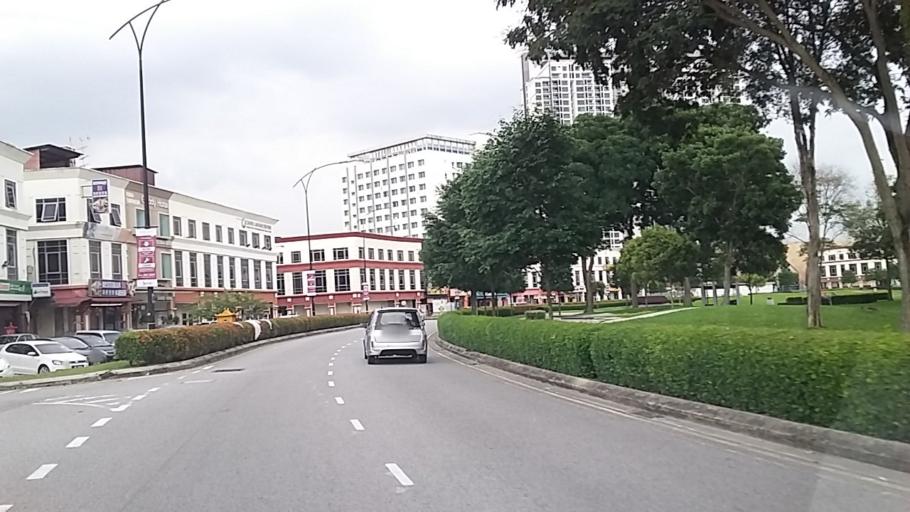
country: MY
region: Johor
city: Skudai
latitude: 1.4797
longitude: 103.6581
